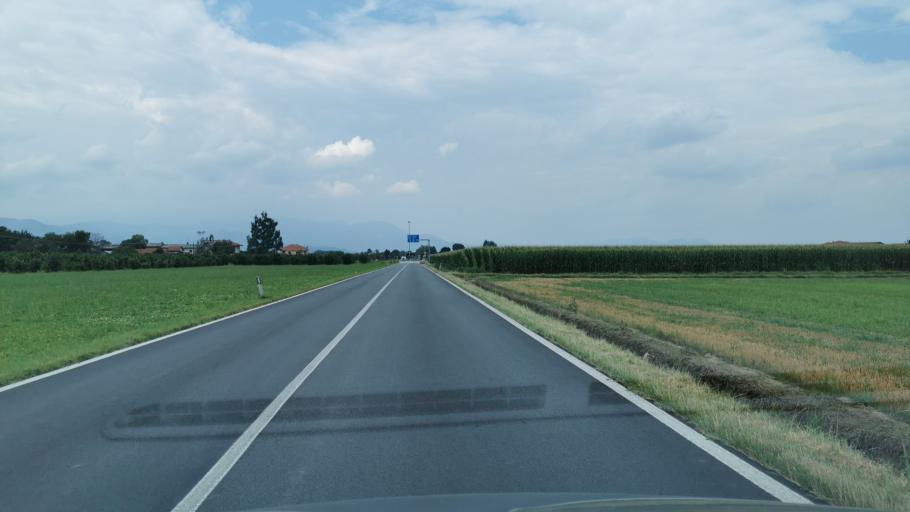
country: IT
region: Piedmont
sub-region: Provincia di Torino
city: Cavour
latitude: 44.8133
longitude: 7.3717
